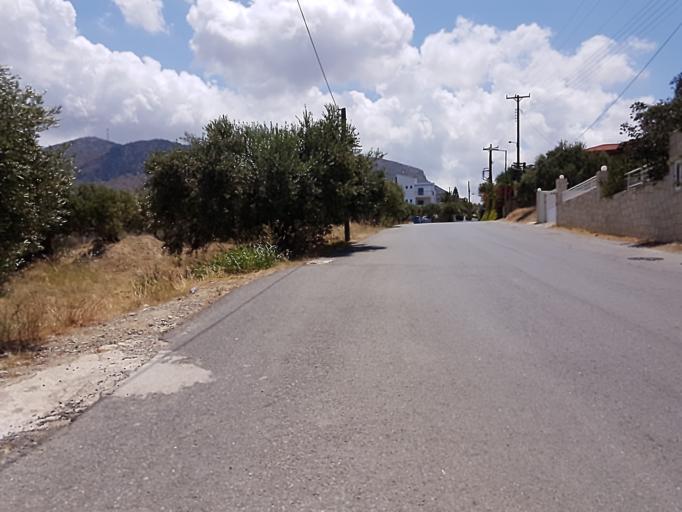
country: GR
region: Crete
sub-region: Nomos Irakleiou
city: Limin Khersonisou
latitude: 35.3174
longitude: 25.3832
